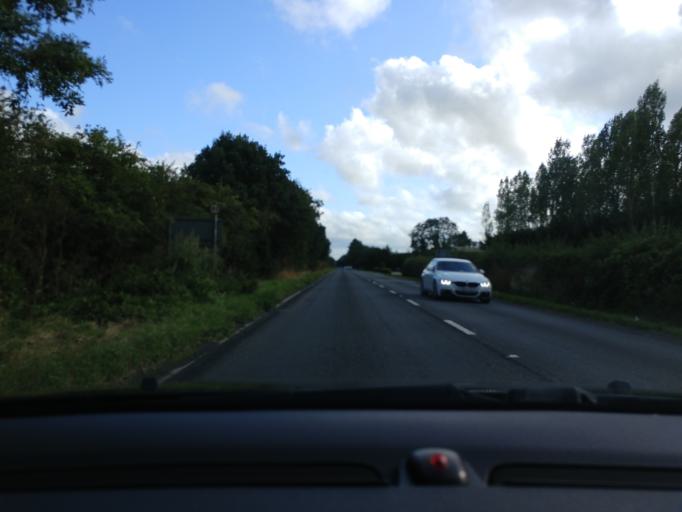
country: GB
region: England
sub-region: Oxfordshire
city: Bicester
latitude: 51.8823
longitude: -1.2292
